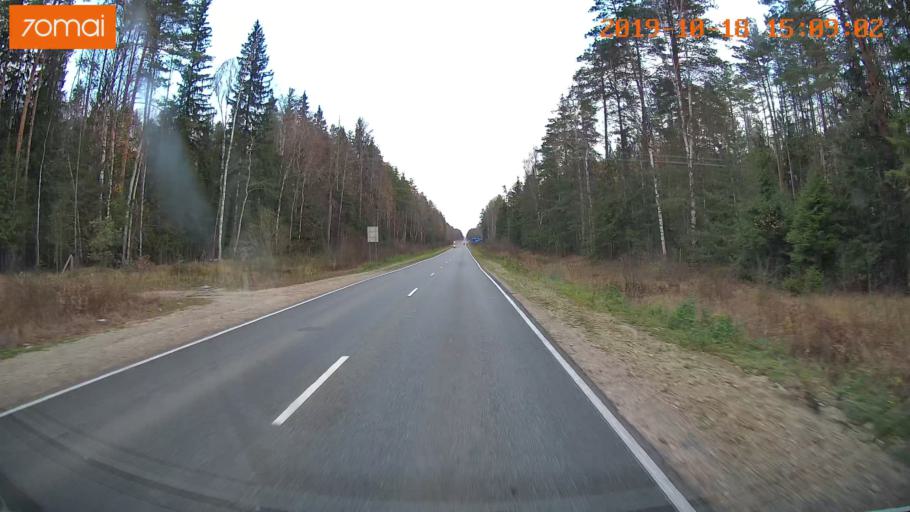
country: RU
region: Vladimir
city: Gus'-Khrustal'nyy
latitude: 55.5607
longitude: 40.6169
